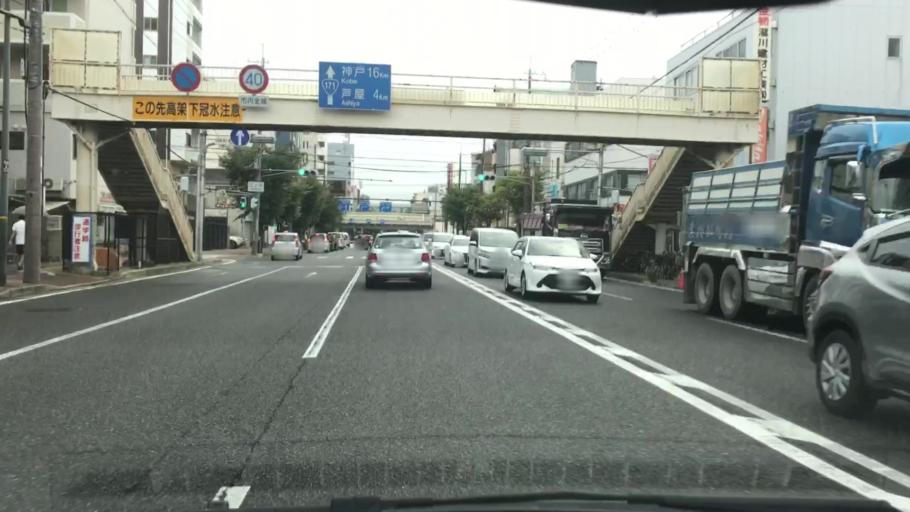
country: JP
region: Hyogo
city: Nishinomiya-hama
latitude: 34.7408
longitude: 135.3393
